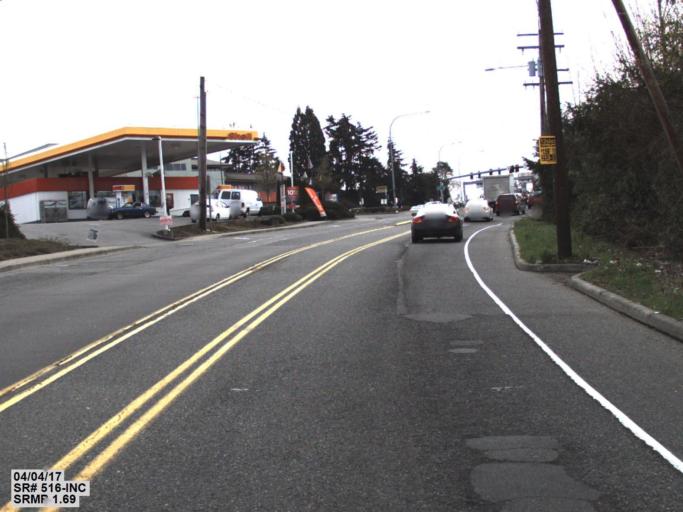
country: US
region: Washington
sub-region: King County
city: Des Moines
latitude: 47.3948
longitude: -122.2961
